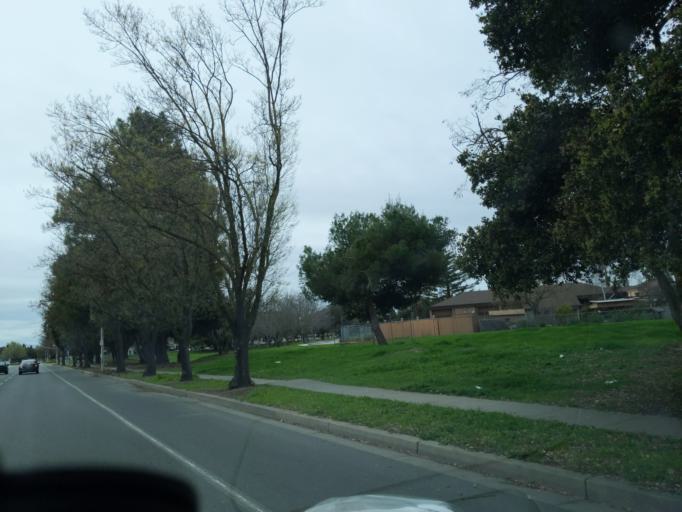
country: US
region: California
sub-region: Alameda County
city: Fremont
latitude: 37.5587
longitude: -121.9602
